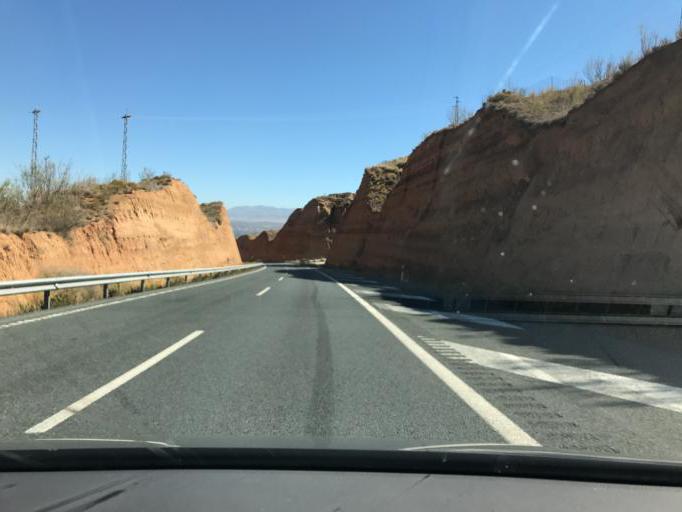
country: ES
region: Andalusia
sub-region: Provincia de Granada
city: Darro
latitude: 37.3238
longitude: -3.2507
